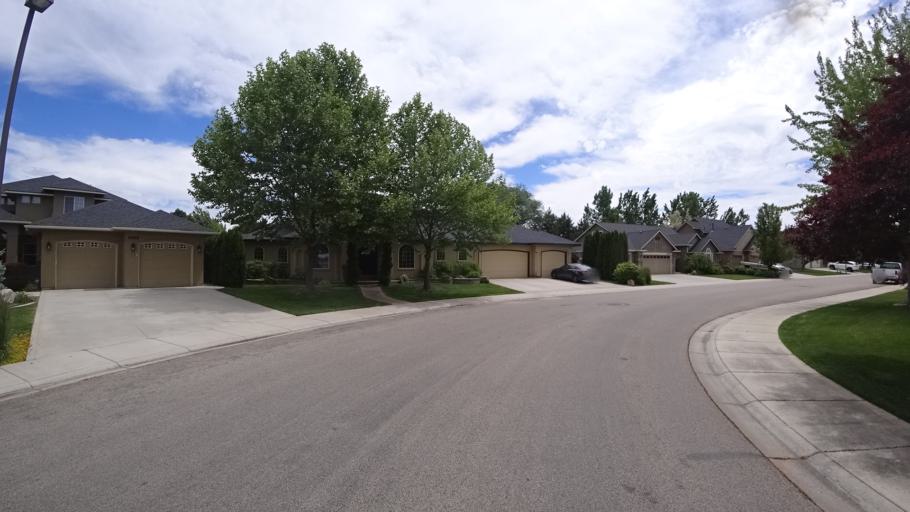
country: US
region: Idaho
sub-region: Ada County
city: Meridian
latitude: 43.6283
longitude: -116.3251
